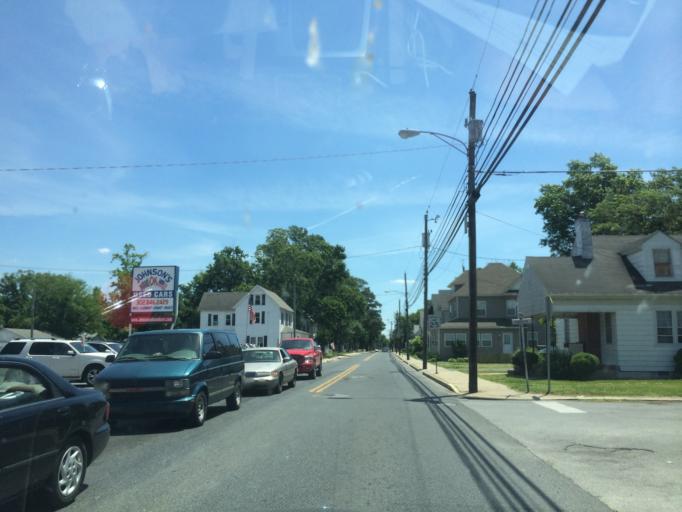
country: US
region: Delaware
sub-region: Sussex County
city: Delmar
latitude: 38.4560
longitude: -75.5738
